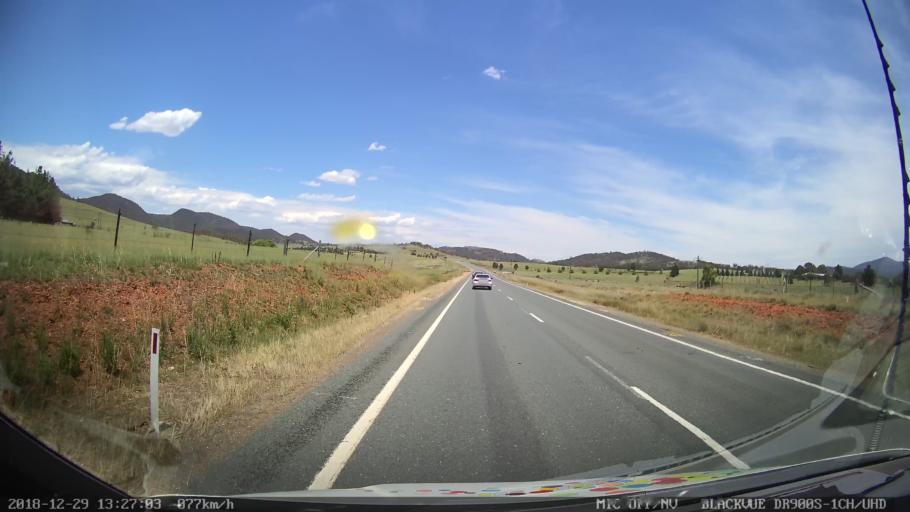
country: AU
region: New South Wales
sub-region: Cooma-Monaro
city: Cooma
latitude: -35.8624
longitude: 149.1586
